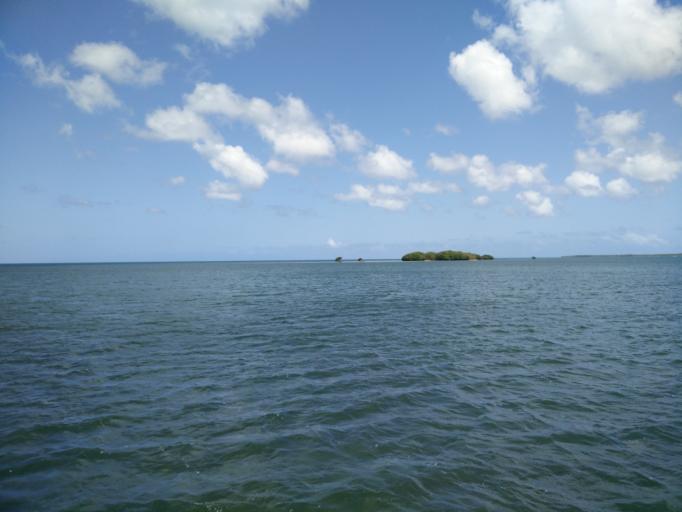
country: GP
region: Guadeloupe
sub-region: Guadeloupe
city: Petit-Canal
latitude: 16.3619
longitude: -61.5027
